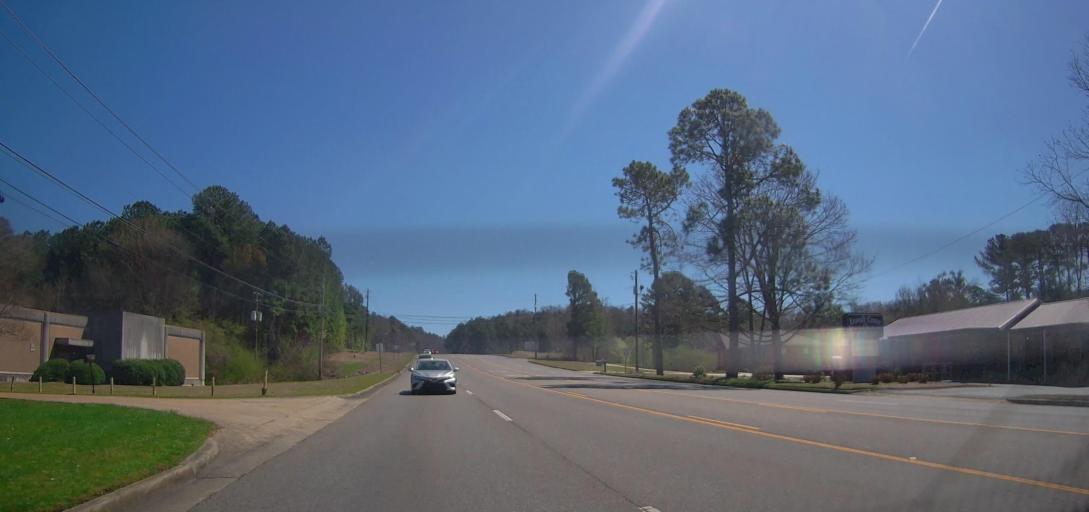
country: US
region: Alabama
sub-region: Etowah County
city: Rainbow City
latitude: 33.9529
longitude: -86.0380
